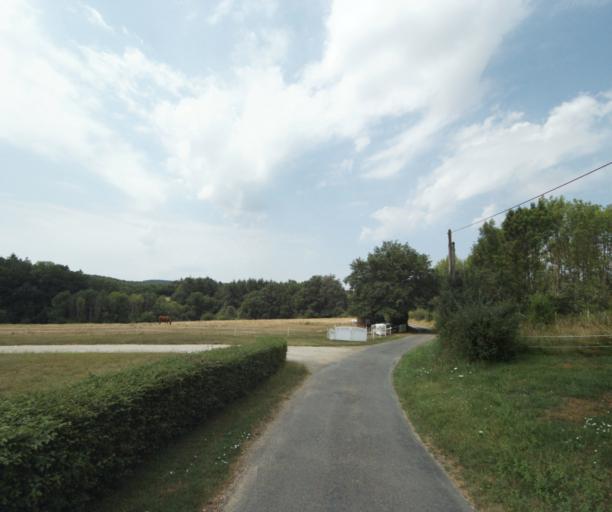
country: FR
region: Bourgogne
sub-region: Departement de Saone-et-Loire
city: Gueugnon
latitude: 46.5801
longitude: 4.0370
